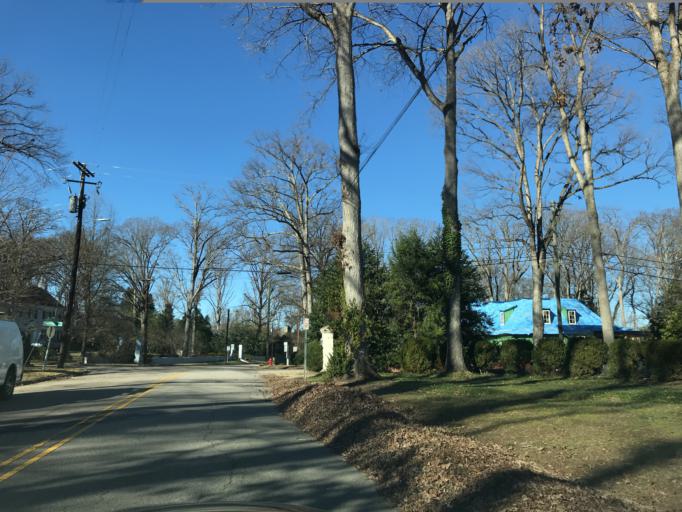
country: US
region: North Carolina
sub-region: Wake County
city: West Raleigh
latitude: 35.8110
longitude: -78.6444
